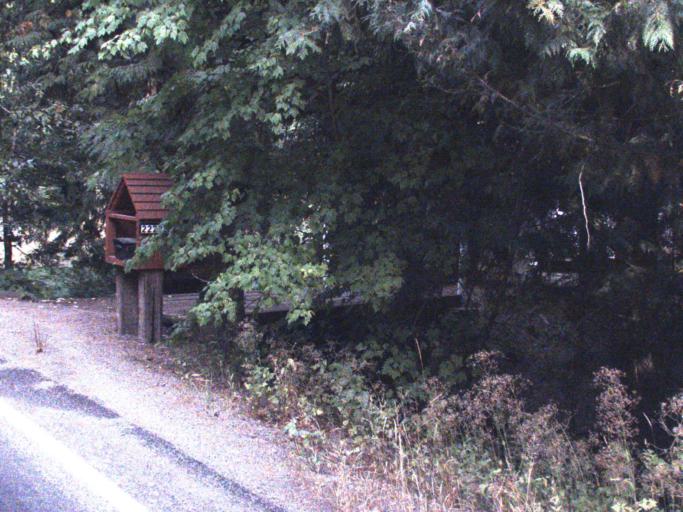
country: US
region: Washington
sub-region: Spokane County
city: Trentwood
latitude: 47.8568
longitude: -117.1631
